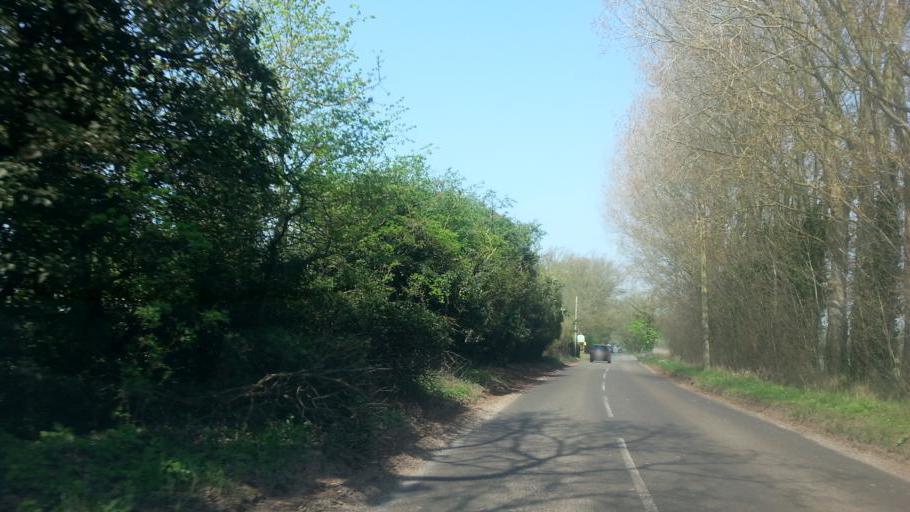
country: GB
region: England
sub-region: Suffolk
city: Thurston
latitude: 52.2402
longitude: 0.8252
